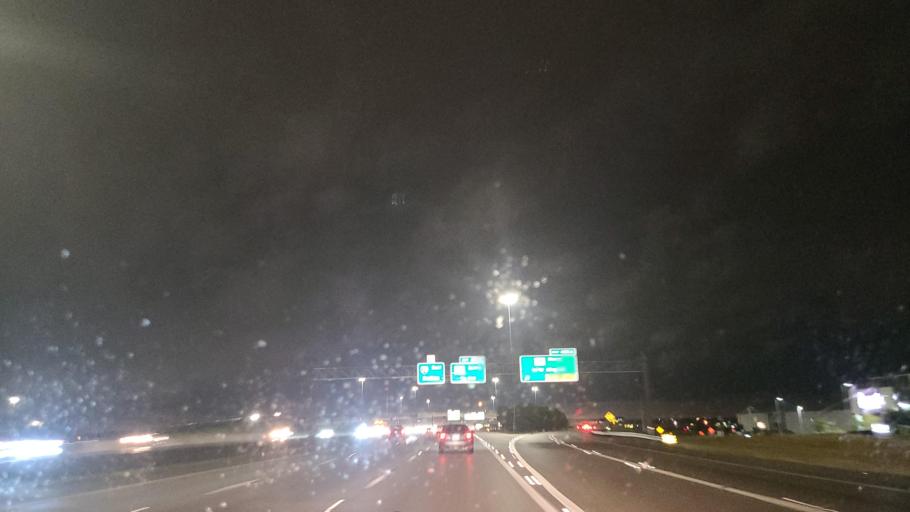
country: US
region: Texas
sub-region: Tarrant County
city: Arlington
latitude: 32.6768
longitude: -97.0707
